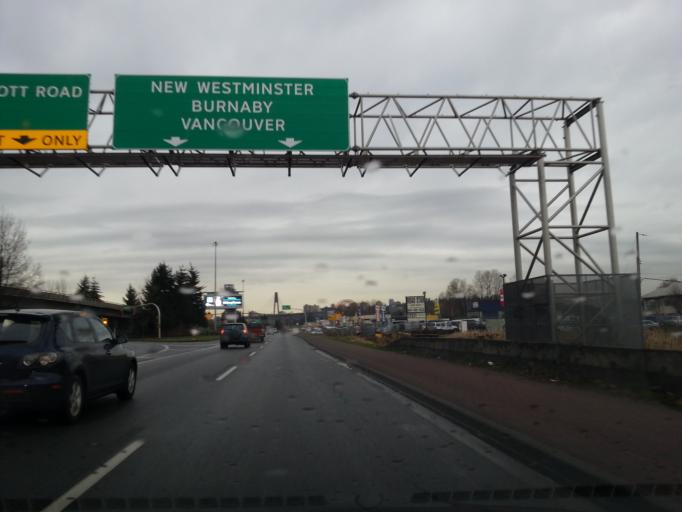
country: CA
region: British Columbia
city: New Westminster
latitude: 49.2063
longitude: -122.8736
